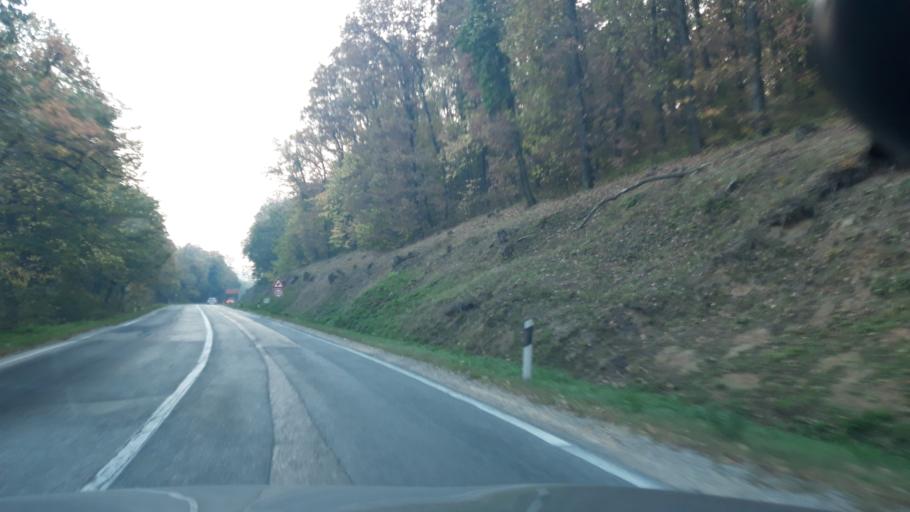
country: RS
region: Autonomna Pokrajina Vojvodina
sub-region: Sremski Okrug
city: Irig
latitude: 45.1413
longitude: 19.8366
